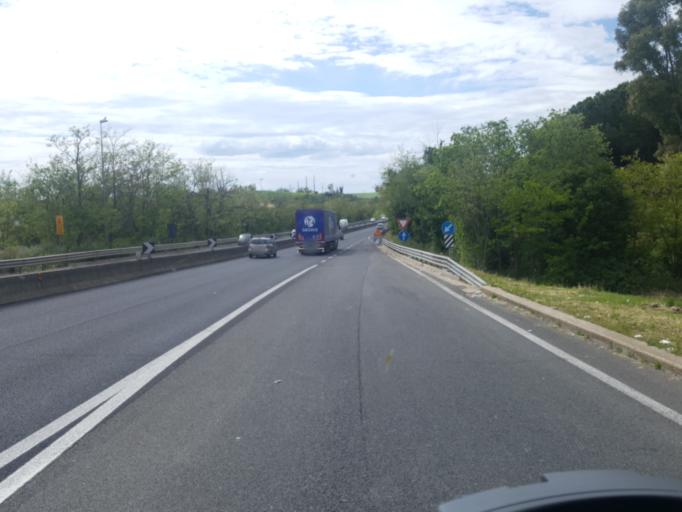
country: IT
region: Latium
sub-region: Citta metropolitana di Roma Capitale
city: La Massimina-Casal Lumbroso
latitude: 41.8830
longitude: 12.3409
